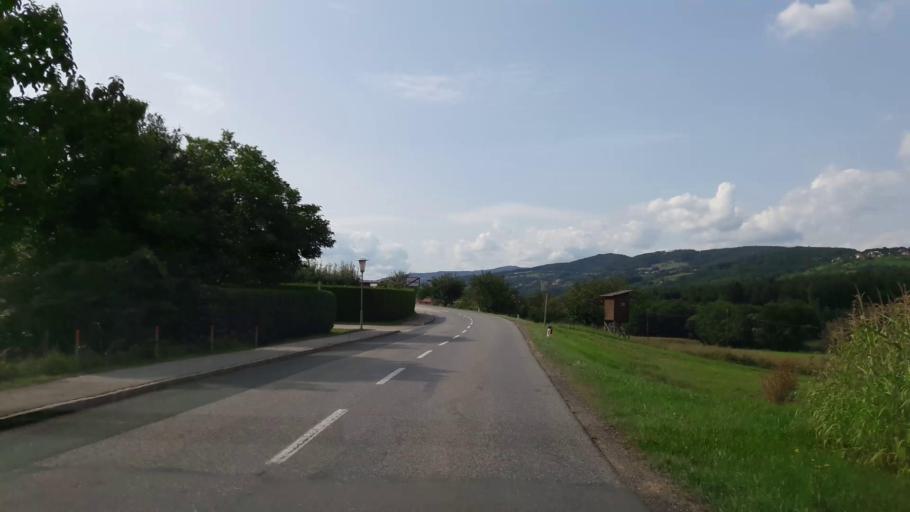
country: AT
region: Styria
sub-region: Politischer Bezirk Hartberg-Fuerstenfeld
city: Dienersdorf
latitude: 47.2201
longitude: 15.8647
